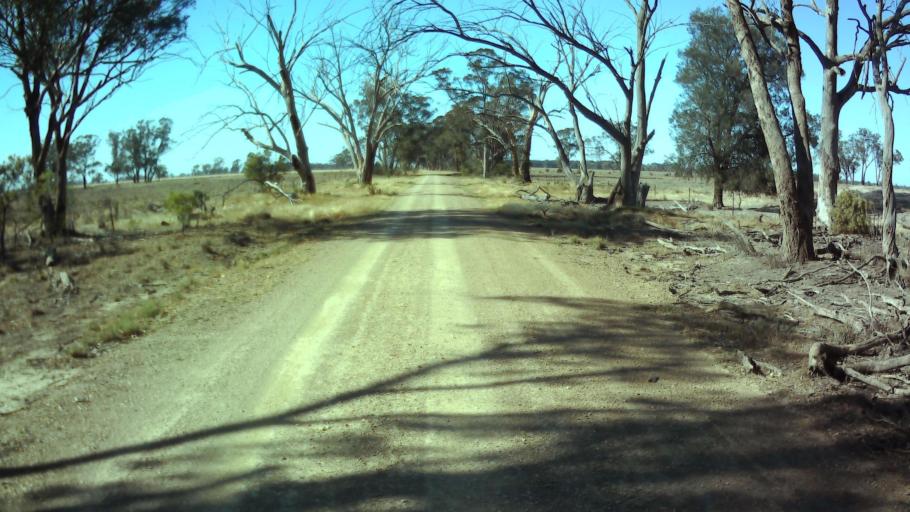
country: AU
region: New South Wales
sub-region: Weddin
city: Grenfell
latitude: -33.9431
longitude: 147.8706
